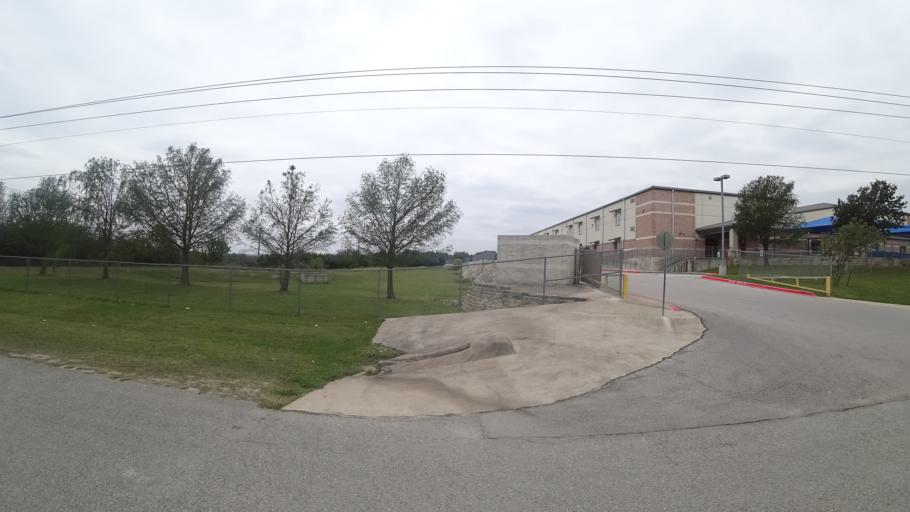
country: US
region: Texas
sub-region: Travis County
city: Lakeway
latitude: 30.3711
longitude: -97.9442
